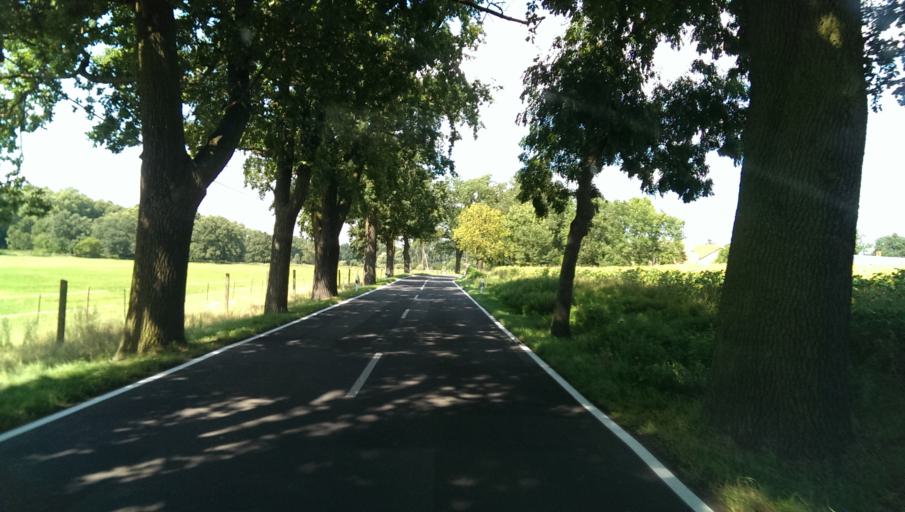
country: DE
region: Brandenburg
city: Trebbin
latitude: 52.2464
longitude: 13.2125
